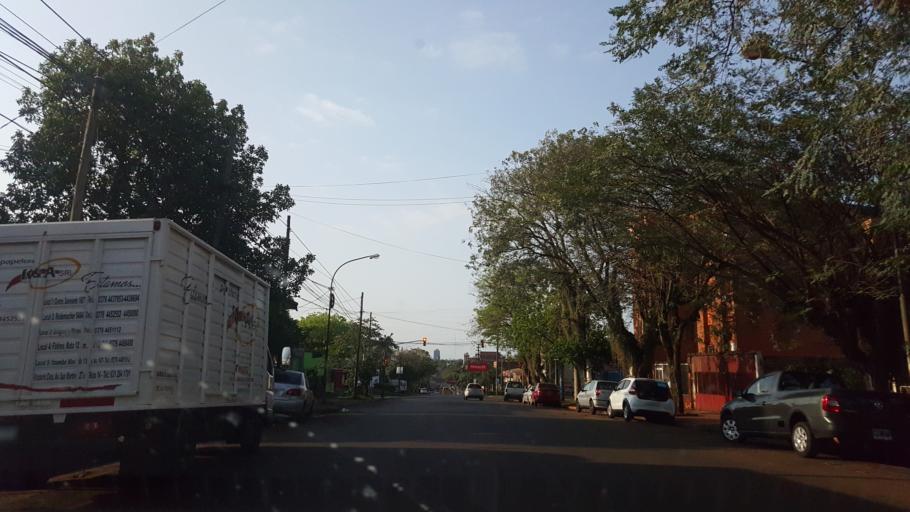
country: AR
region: Misiones
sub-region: Departamento de Capital
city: Posadas
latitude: -27.3991
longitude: -55.8981
